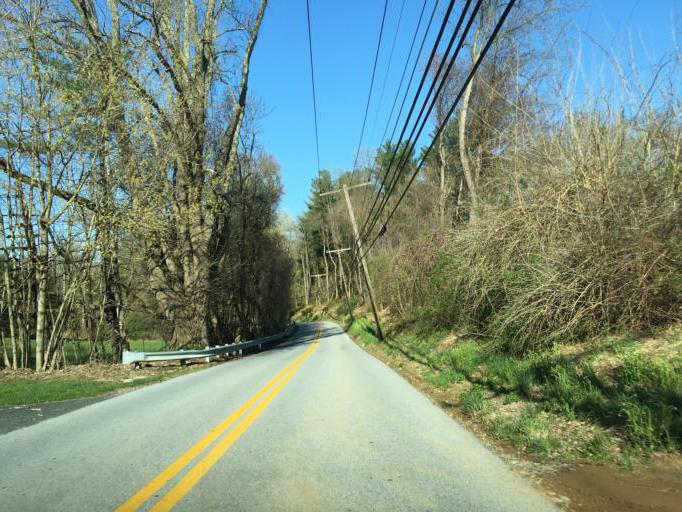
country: US
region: Maryland
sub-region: Baltimore County
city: Hunt Valley
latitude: 39.5432
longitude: -76.6294
